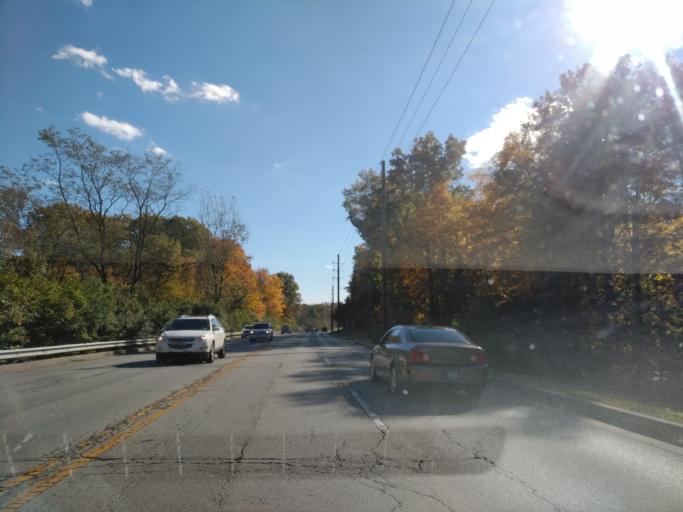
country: US
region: Indiana
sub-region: Marion County
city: Lawrence
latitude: 39.8726
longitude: -86.0457
